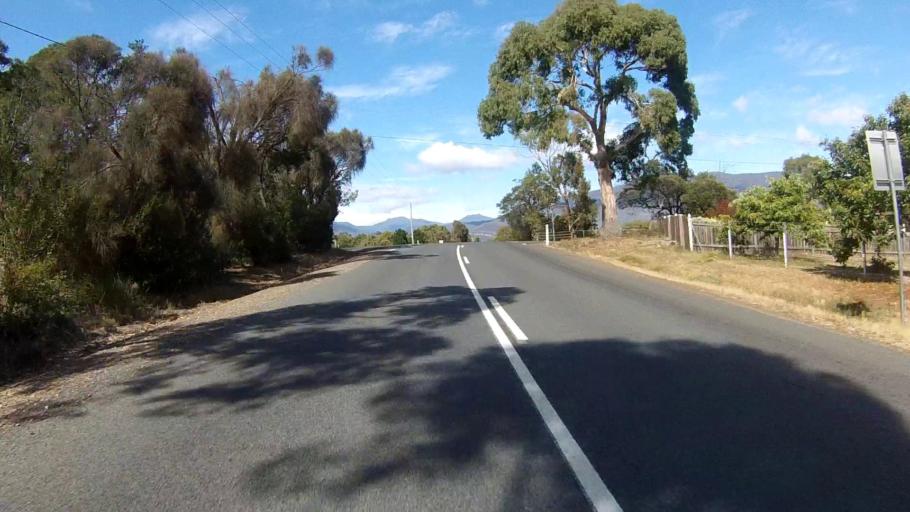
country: AU
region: Tasmania
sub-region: Brighton
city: Old Beach
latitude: -42.7682
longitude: 147.2732
